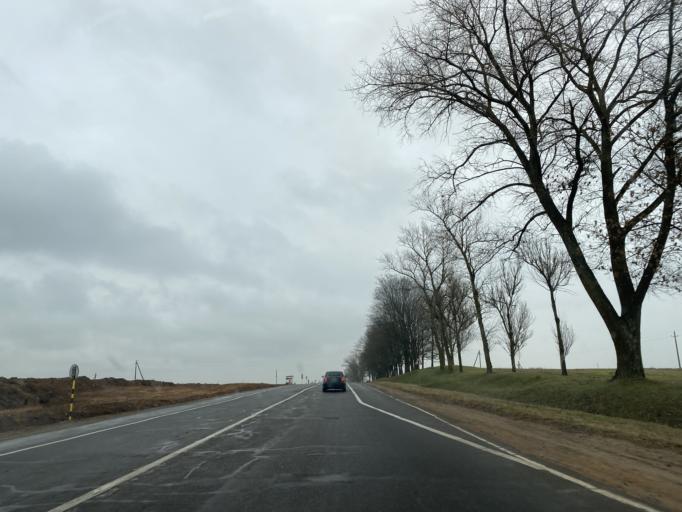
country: BY
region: Minsk
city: Slabada
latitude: 54.0238
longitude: 27.9354
